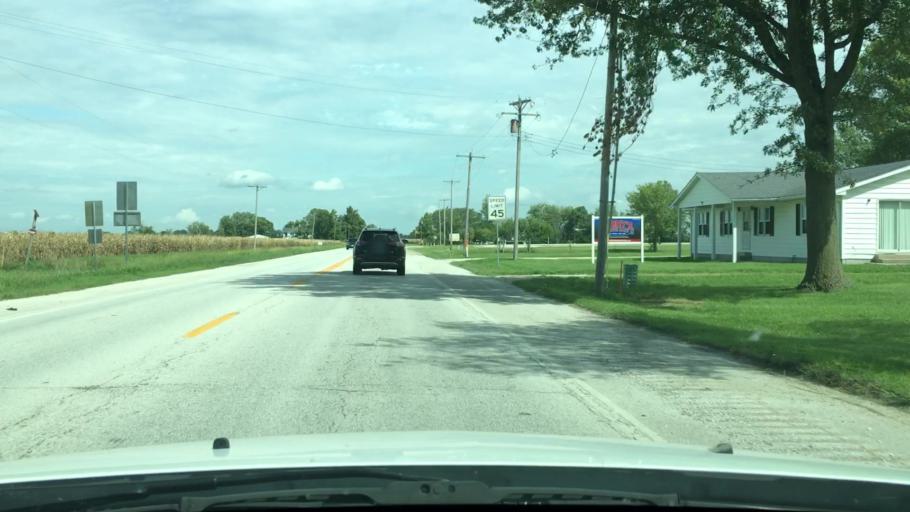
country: US
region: Missouri
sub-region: Audrain County
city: Vandalia
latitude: 39.2478
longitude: -91.6453
